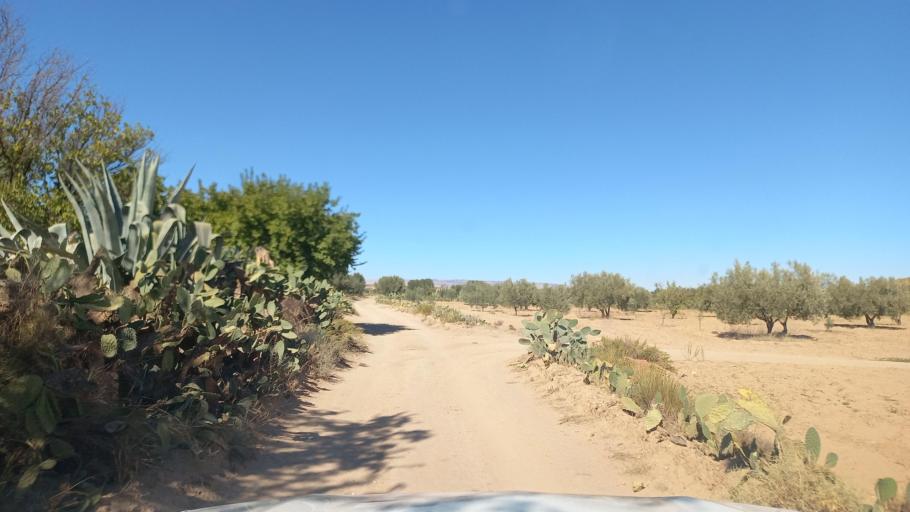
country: TN
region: Al Qasrayn
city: Sbiba
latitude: 35.4001
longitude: 9.0861
